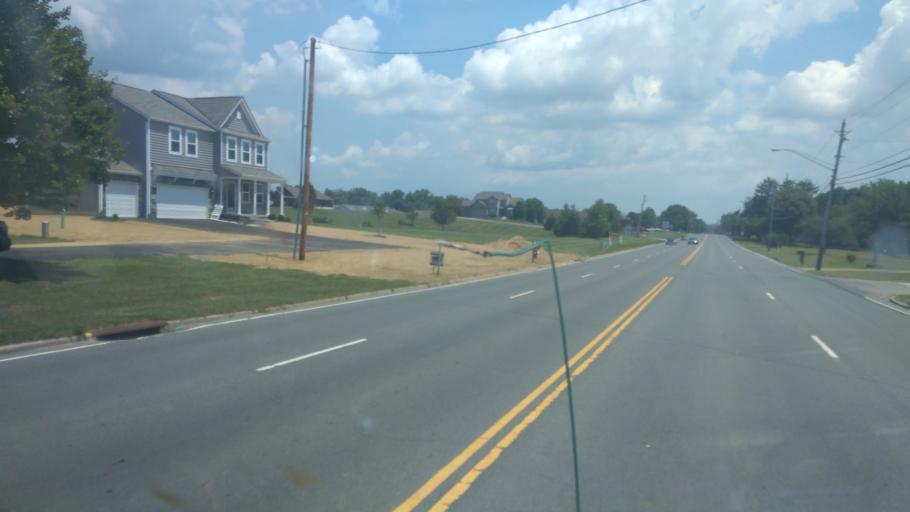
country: US
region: Ohio
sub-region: Fairfield County
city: Lancaster
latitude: 39.7261
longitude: -82.6461
